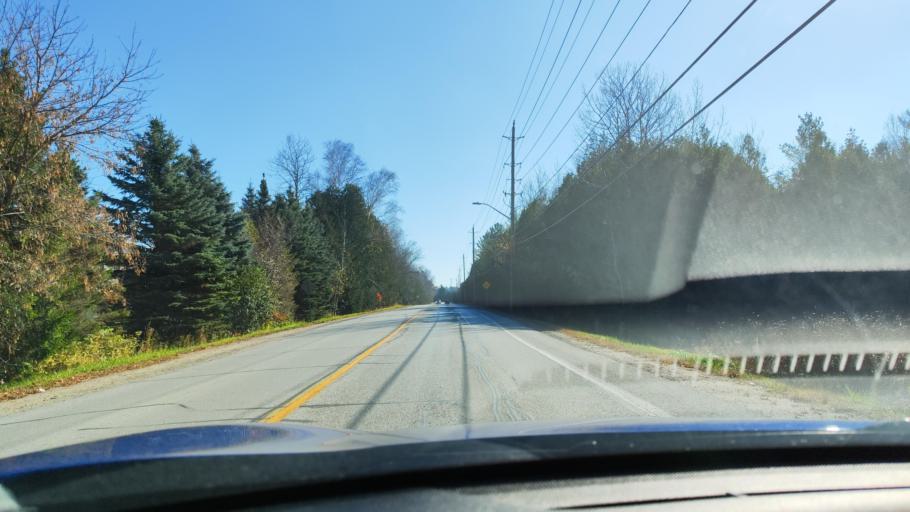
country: CA
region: Ontario
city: Wasaga Beach
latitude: 44.5095
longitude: -79.9965
